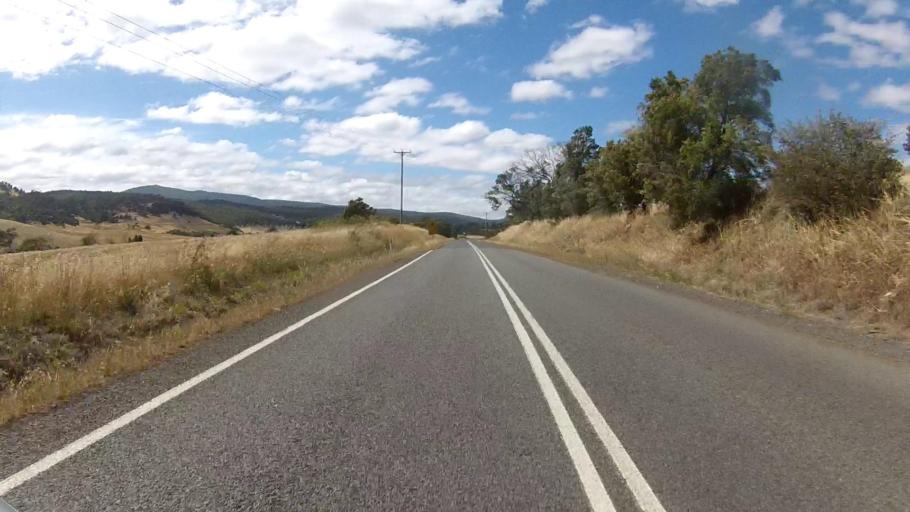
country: AU
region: Tasmania
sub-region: Sorell
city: Sorell
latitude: -42.6057
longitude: 147.4192
